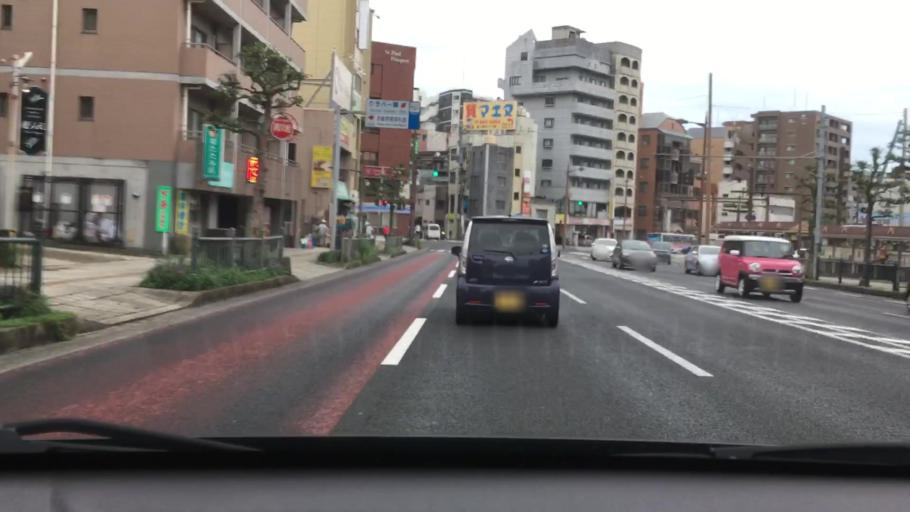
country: JP
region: Nagasaki
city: Nagasaki-shi
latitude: 32.7711
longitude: 129.8636
